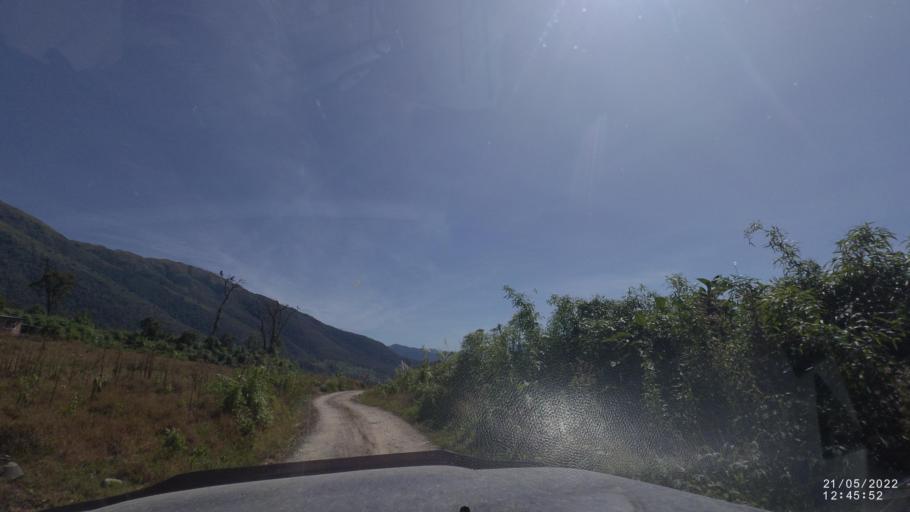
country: BO
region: Cochabamba
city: Colomi
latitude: -17.1863
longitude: -65.9363
